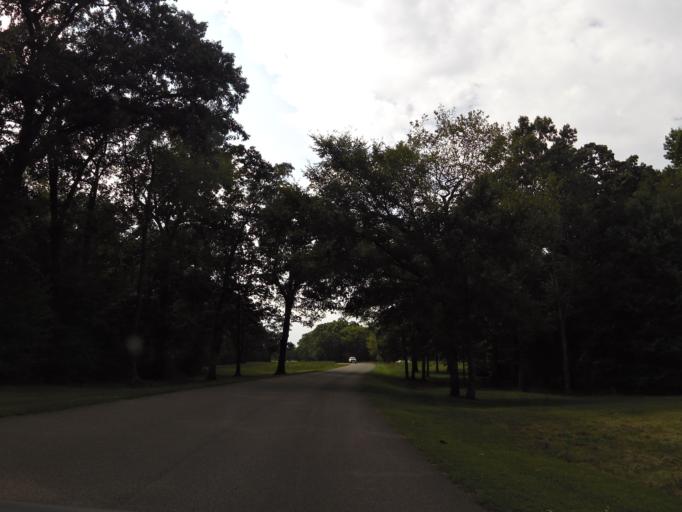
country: US
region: Tennessee
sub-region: Hardin County
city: Crump
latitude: 35.1521
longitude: -88.3313
